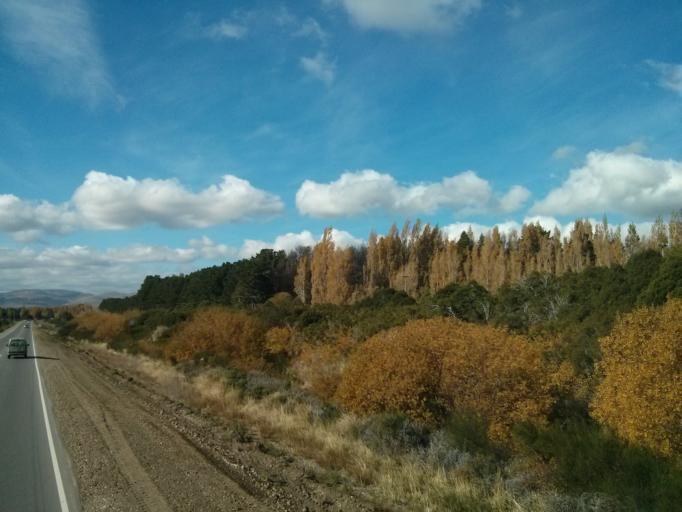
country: AR
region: Rio Negro
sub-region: Departamento de Bariloche
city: San Carlos de Bariloche
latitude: -41.1075
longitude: -71.2113
